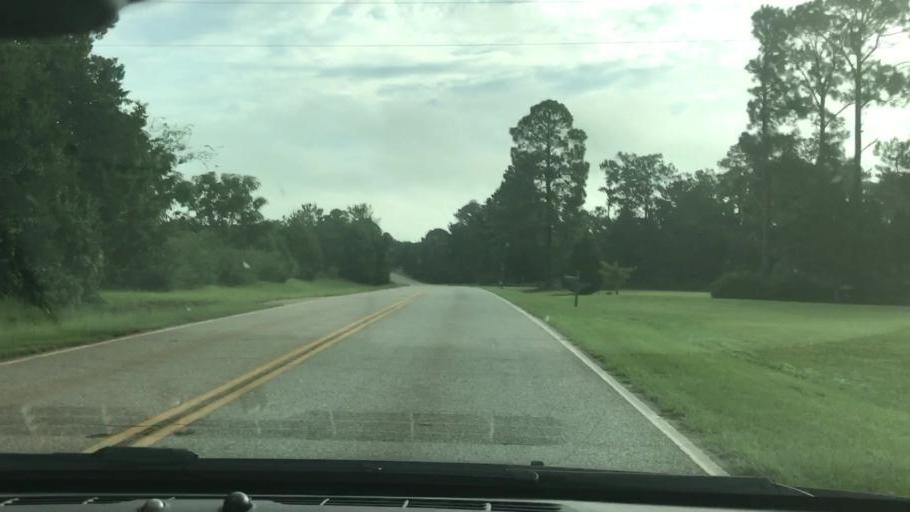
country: US
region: Georgia
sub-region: Quitman County
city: Georgetown
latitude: 31.9028
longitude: -85.0413
